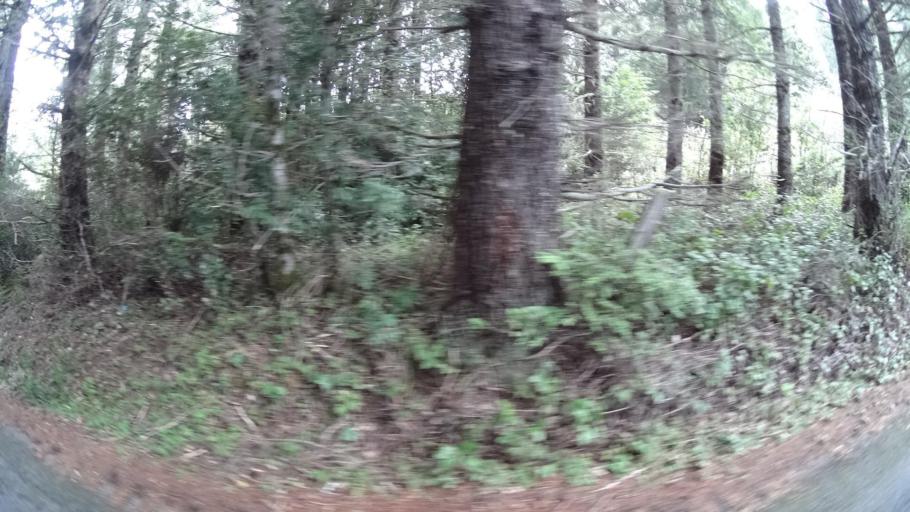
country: US
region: California
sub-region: Humboldt County
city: Blue Lake
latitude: 40.7934
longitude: -123.9717
